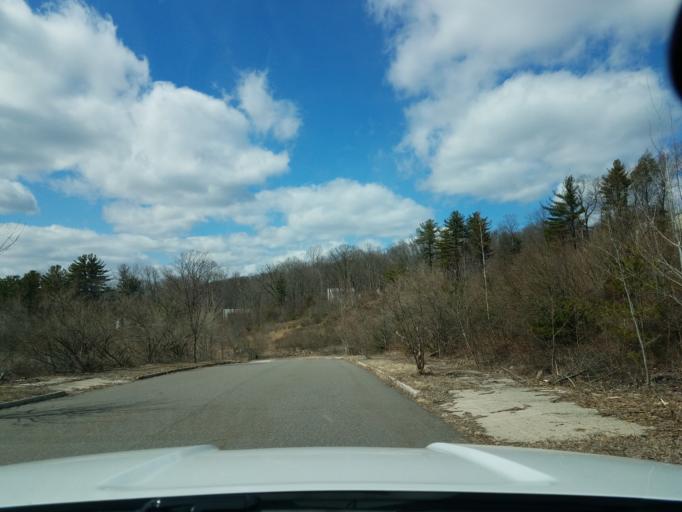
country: US
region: Connecticut
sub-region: New Haven County
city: Naugatuck
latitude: 41.4726
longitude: -73.0291
